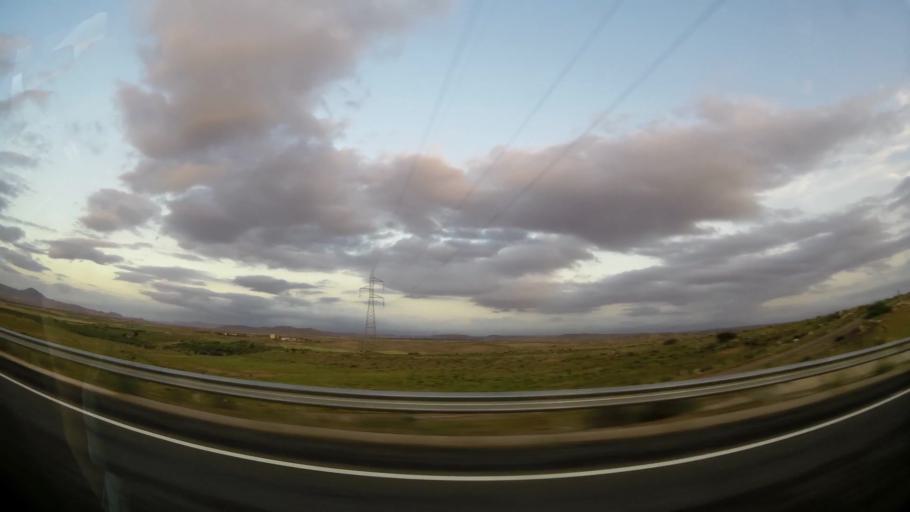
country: MA
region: Oriental
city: Taourirt
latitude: 34.5996
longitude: -2.7748
